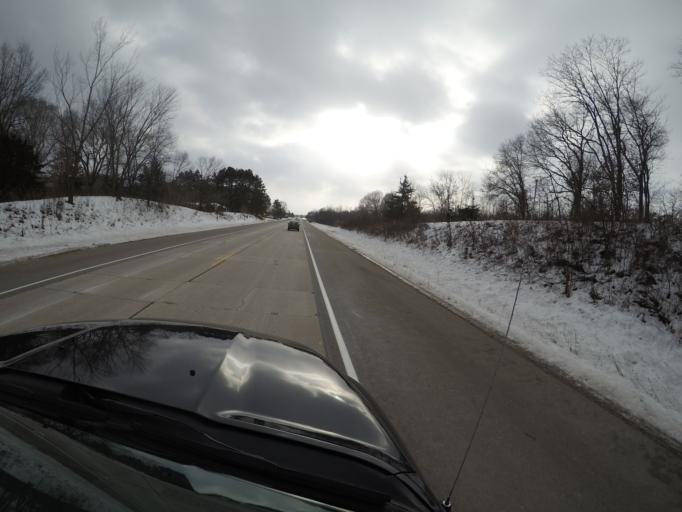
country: US
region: Wisconsin
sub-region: Trempealeau County
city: Galesville
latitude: 44.0384
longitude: -91.2907
